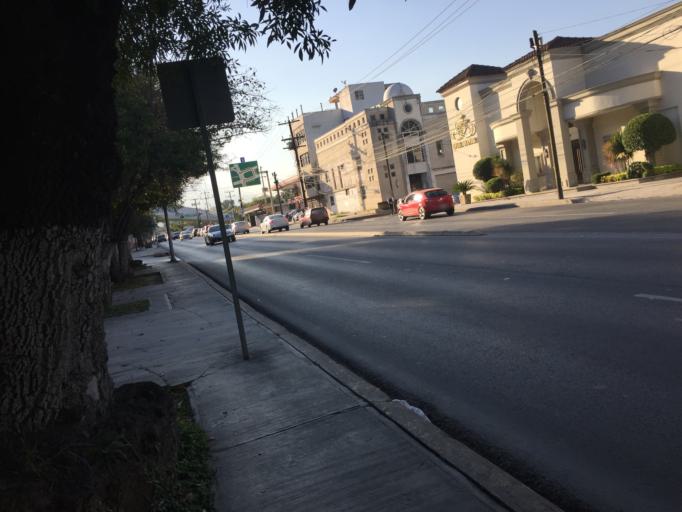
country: MX
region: Nuevo Leon
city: Garza Garcia
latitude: 25.6516
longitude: -100.3695
